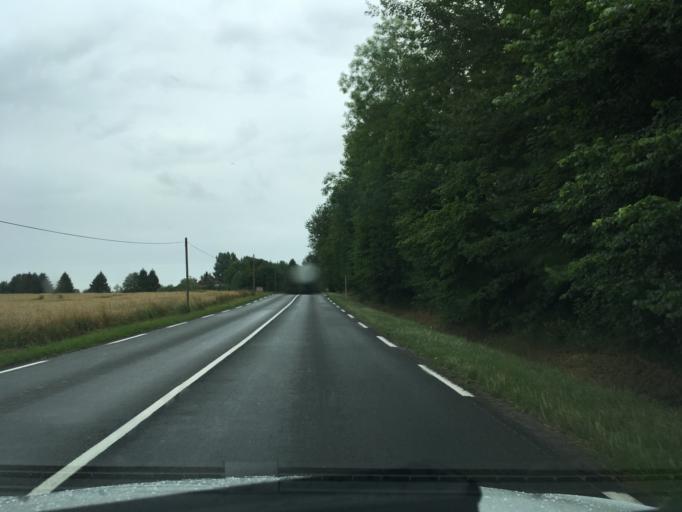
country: FR
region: Picardie
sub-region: Departement de l'Aisne
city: Esqueheries
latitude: 49.9451
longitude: 3.7657
